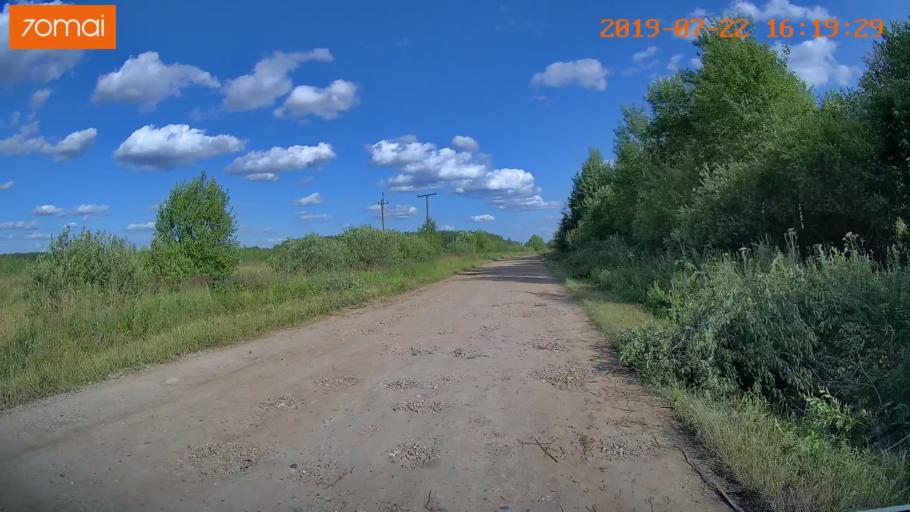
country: RU
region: Ivanovo
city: Novo-Talitsy
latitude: 57.0662
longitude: 40.8914
